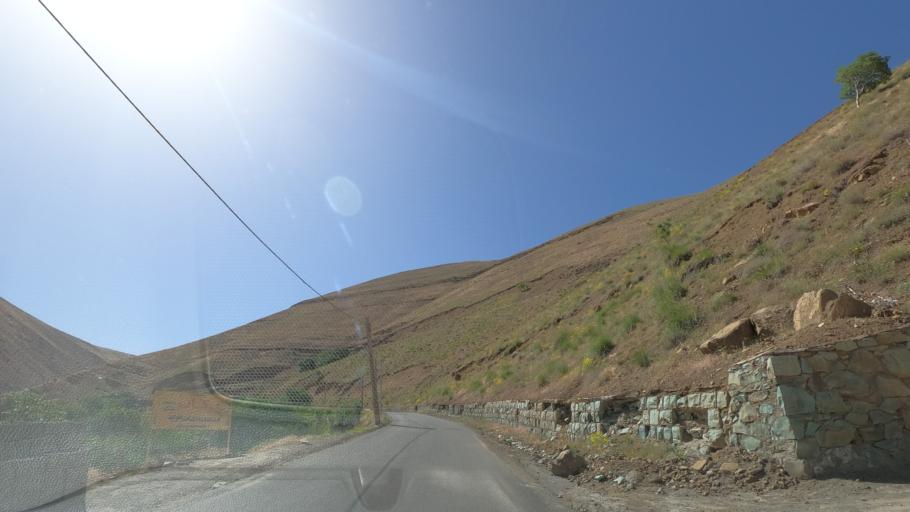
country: IR
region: Alborz
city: Karaj
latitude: 35.9414
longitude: 51.0840
